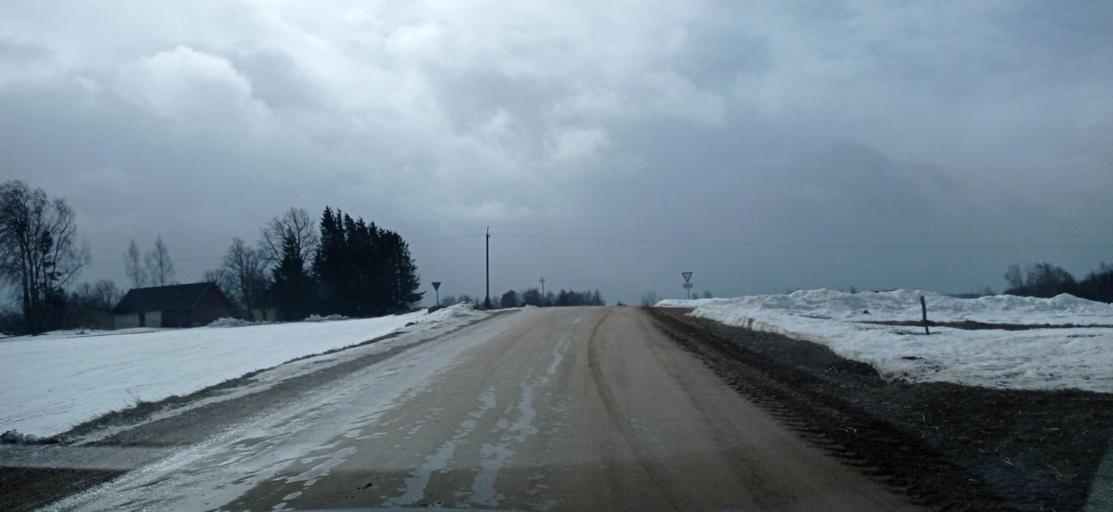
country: EE
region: Tartu
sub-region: Noo vald
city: Noo
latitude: 58.0883
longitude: 26.6592
